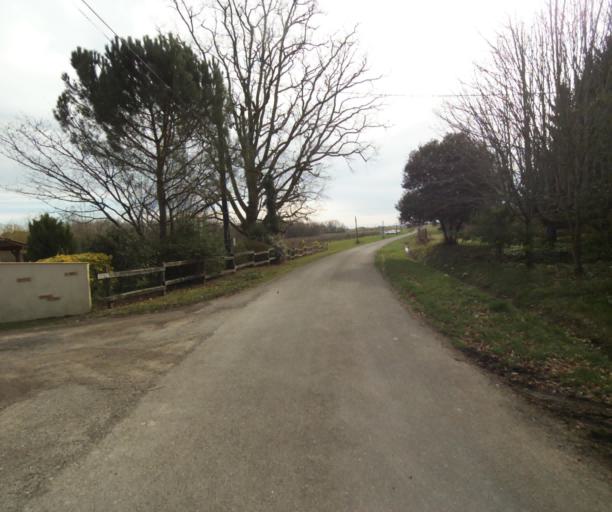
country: FR
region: Aquitaine
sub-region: Departement des Landes
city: Gabarret
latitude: 43.9280
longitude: 0.0453
